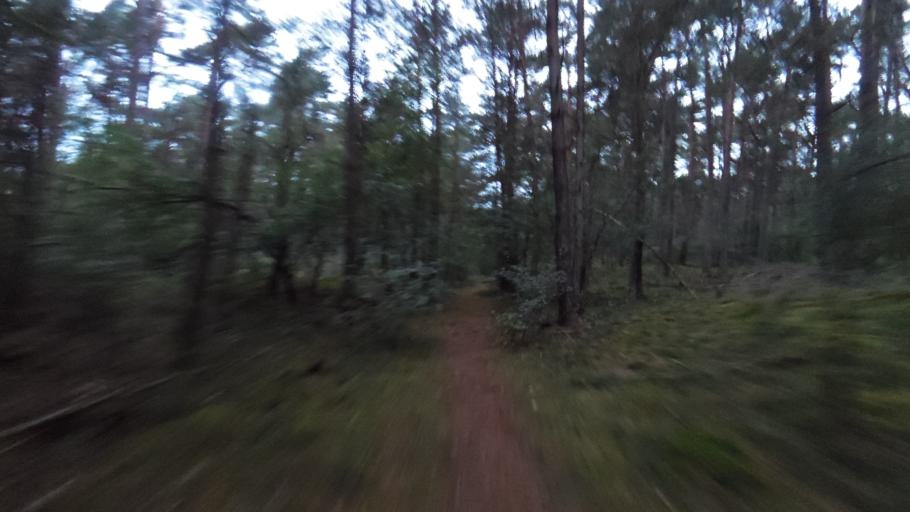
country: NL
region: Gelderland
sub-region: Gemeente Ede
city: Harskamp
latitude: 52.1679
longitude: 5.7504
